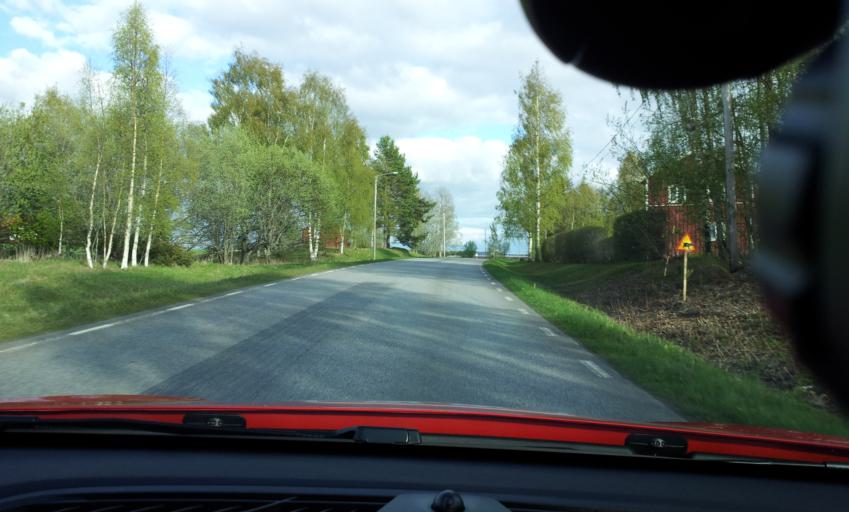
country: SE
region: Jaemtland
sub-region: Krokoms Kommun
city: Krokom
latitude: 63.2666
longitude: 14.3913
